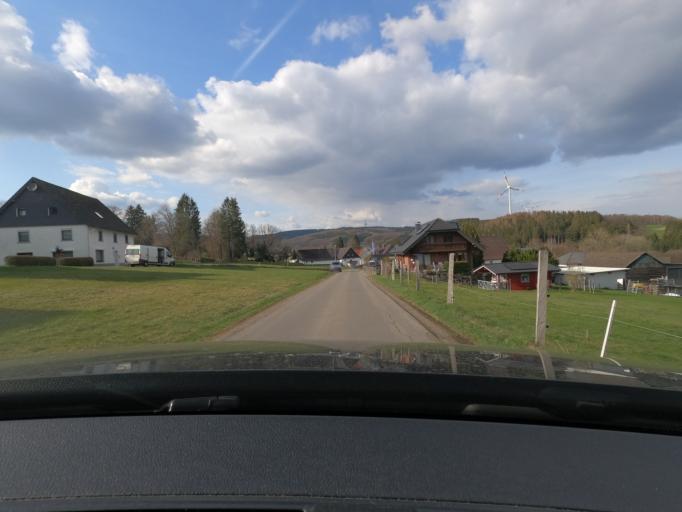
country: DE
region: North Rhine-Westphalia
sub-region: Regierungsbezirk Arnsberg
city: Herscheid
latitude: 51.1142
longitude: 7.7769
